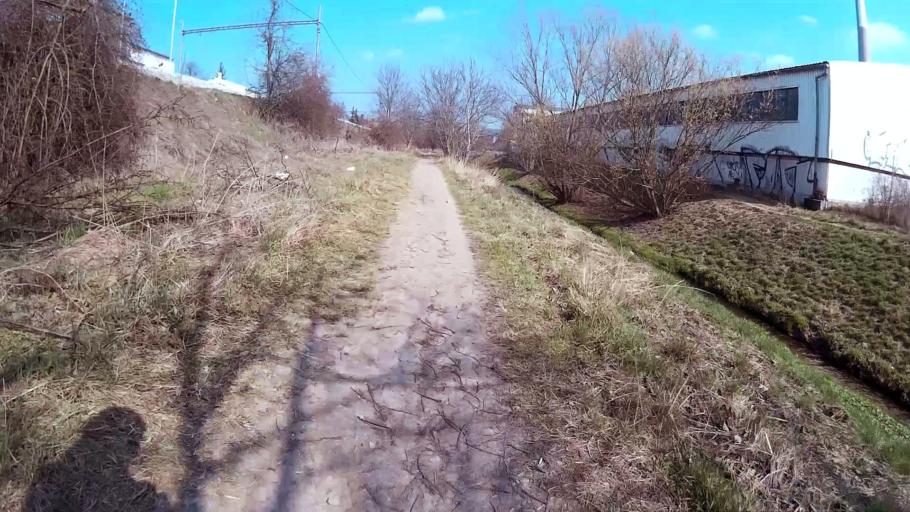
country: CZ
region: South Moravian
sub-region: Mesto Brno
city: Mokra Hora
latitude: 49.2485
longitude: 16.5902
